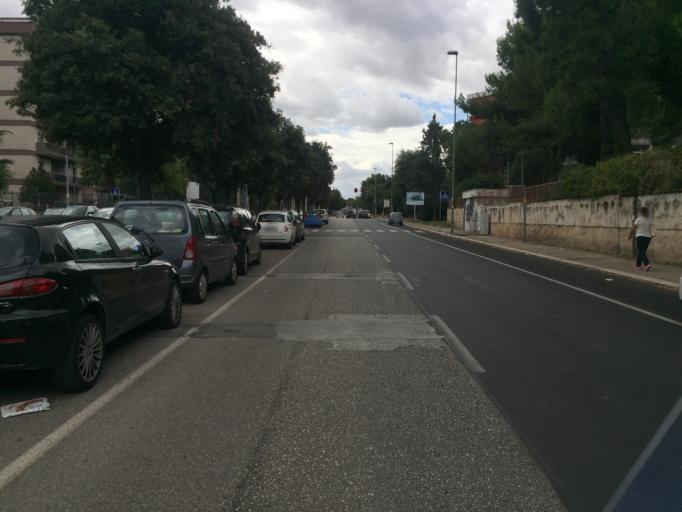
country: IT
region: Apulia
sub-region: Provincia di Bari
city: Bari
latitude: 41.0946
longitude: 16.8642
